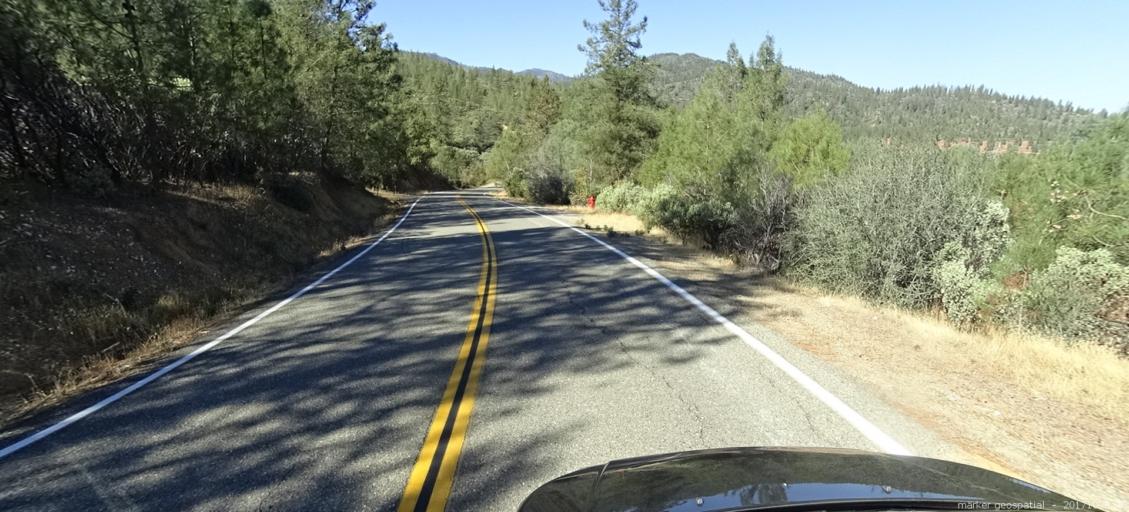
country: US
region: California
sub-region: Shasta County
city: Shasta
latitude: 40.6209
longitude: -122.4661
